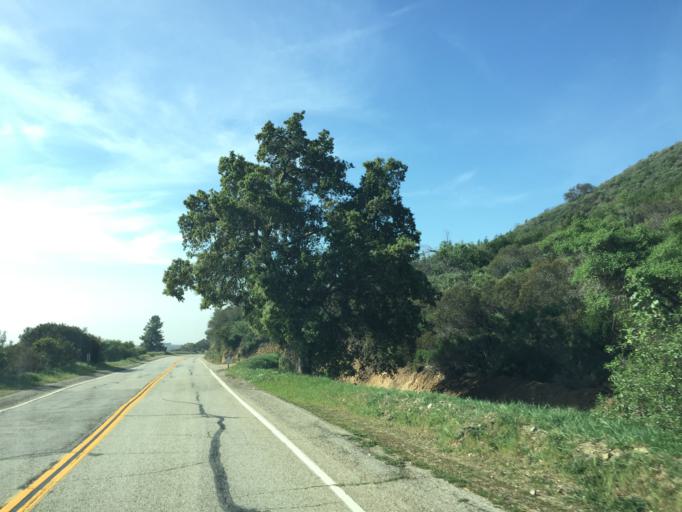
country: US
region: California
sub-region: San Bernardino County
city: San Antonio Heights
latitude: 34.1671
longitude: -117.6794
